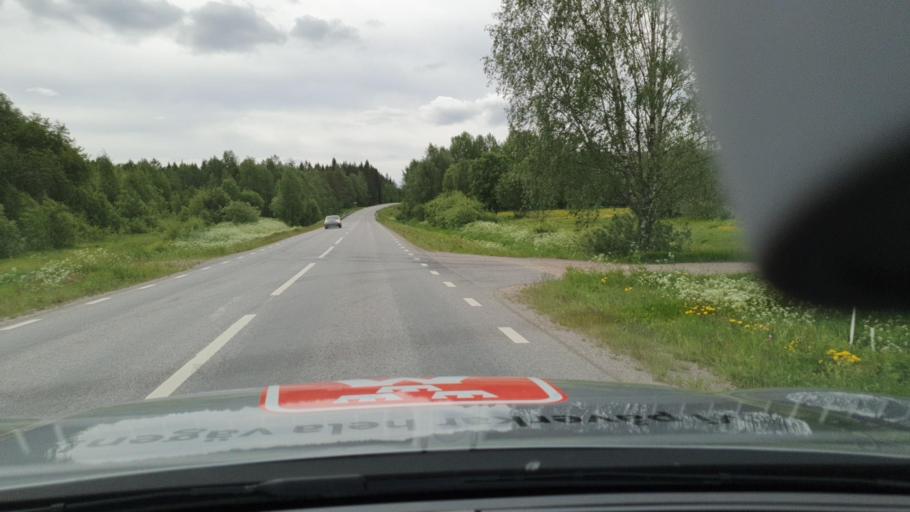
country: SE
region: Norrbotten
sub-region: Kalix Kommun
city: Kalix
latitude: 65.9186
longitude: 23.4595
